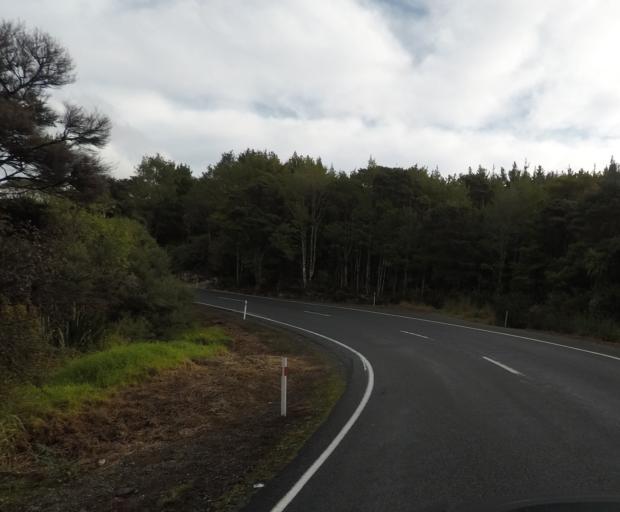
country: NZ
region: Northland
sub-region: Whangarei
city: Ruakaka
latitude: -36.0535
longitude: 174.5497
